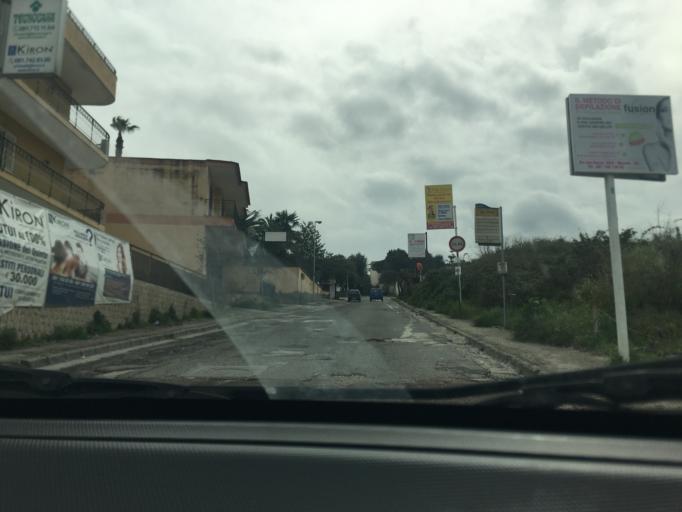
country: IT
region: Campania
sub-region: Provincia di Napoli
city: Marano di Napoli
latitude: 40.8951
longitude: 14.1814
